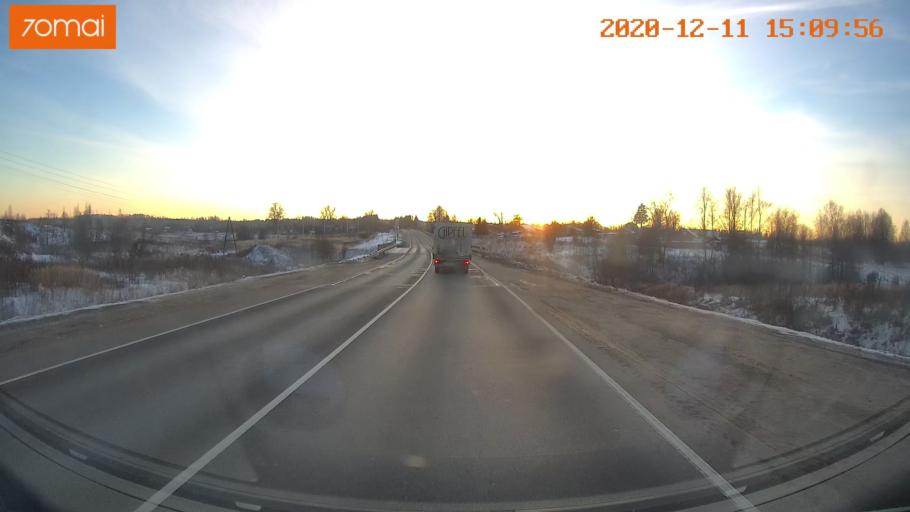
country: RU
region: Ivanovo
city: Furmanov
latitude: 57.2877
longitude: 41.1639
